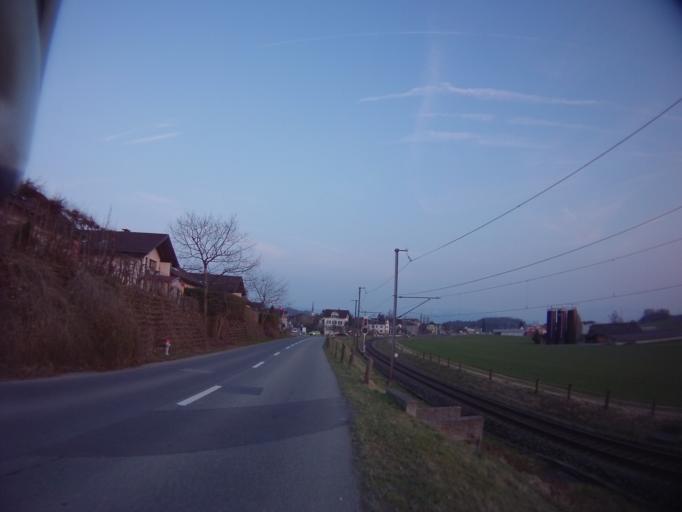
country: CH
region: Zurich
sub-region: Bezirk Affoltern
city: Mettmenstetten
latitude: 47.2493
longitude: 8.4540
